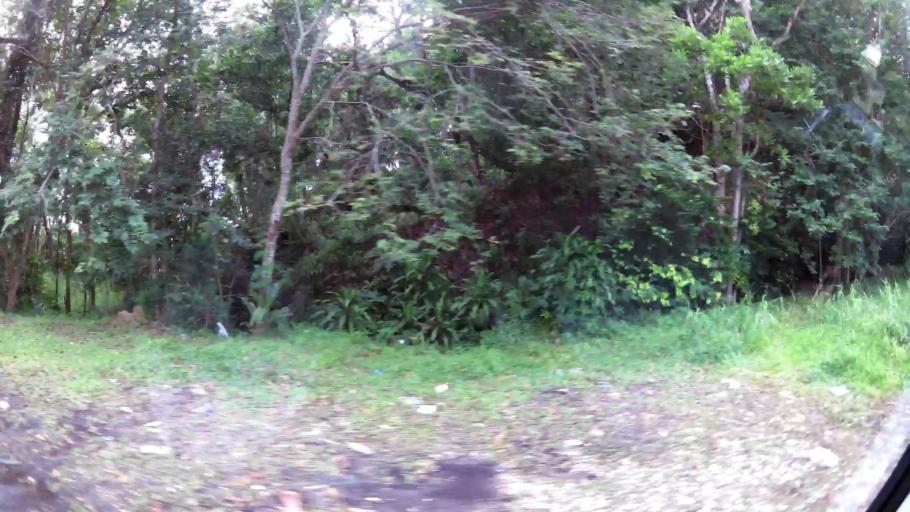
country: BN
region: Brunei and Muara
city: Bandar Seri Begawan
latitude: 4.8889
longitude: 114.9241
